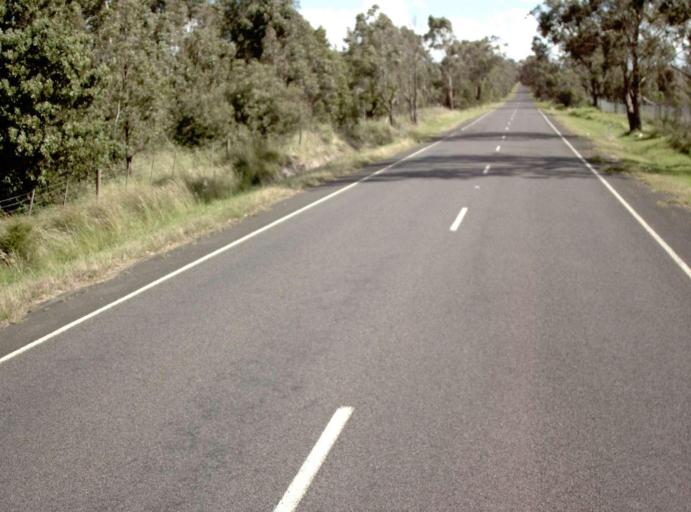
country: AU
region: Victoria
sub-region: Latrobe
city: Morwell
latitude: -38.1743
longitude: 146.4059
